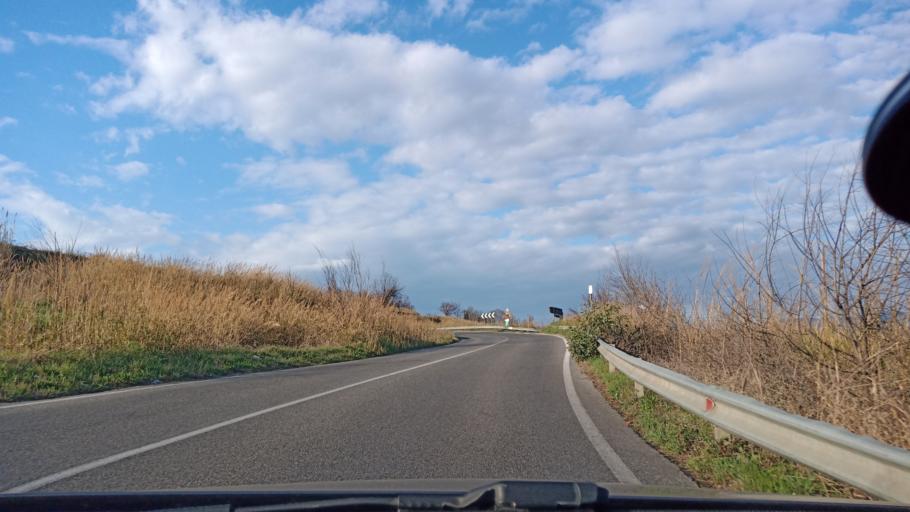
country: IT
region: Latium
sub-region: Citta metropolitana di Roma Capitale
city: Nazzano
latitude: 42.2027
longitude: 12.6049
